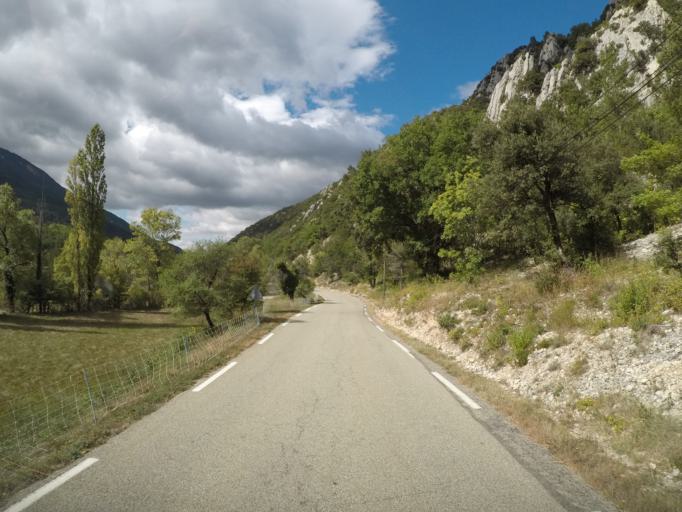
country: FR
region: Rhone-Alpes
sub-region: Departement de la Drome
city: Buis-les-Baronnies
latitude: 44.1928
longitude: 5.3301
